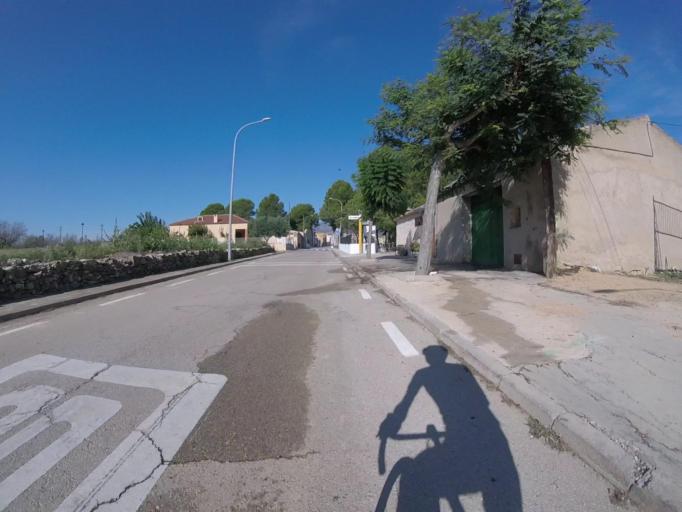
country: ES
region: Valencia
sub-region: Provincia de Castello
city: Sarratella
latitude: 40.2620
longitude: 0.0731
